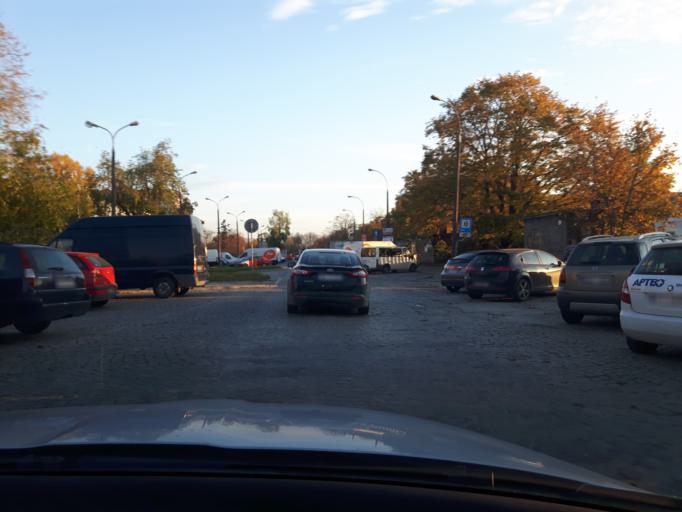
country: PL
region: Masovian Voivodeship
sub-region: Warszawa
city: Ochota
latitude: 52.2236
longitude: 20.9536
